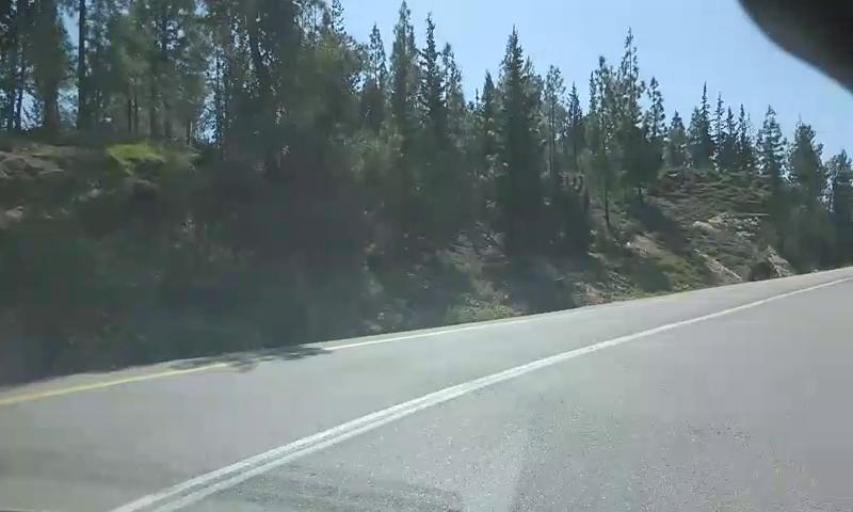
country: PS
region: West Bank
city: Nahhalin
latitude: 31.6749
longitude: 35.1065
